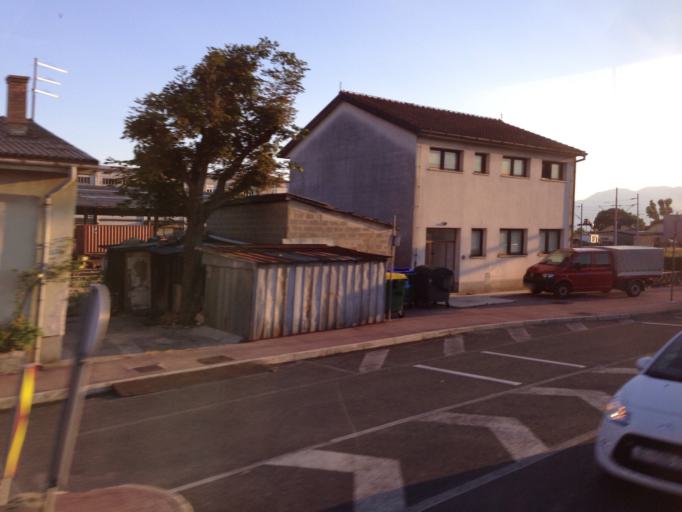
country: HR
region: Primorsko-Goranska
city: Drenova
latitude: 45.3235
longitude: 14.4525
